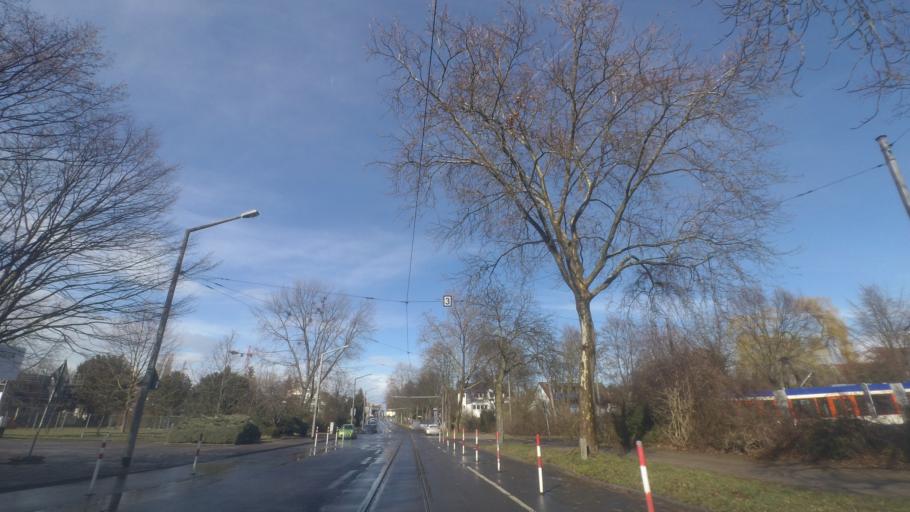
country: DE
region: Hesse
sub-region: Regierungsbezirk Darmstadt
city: Darmstadt
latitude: 49.8504
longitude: 8.6532
